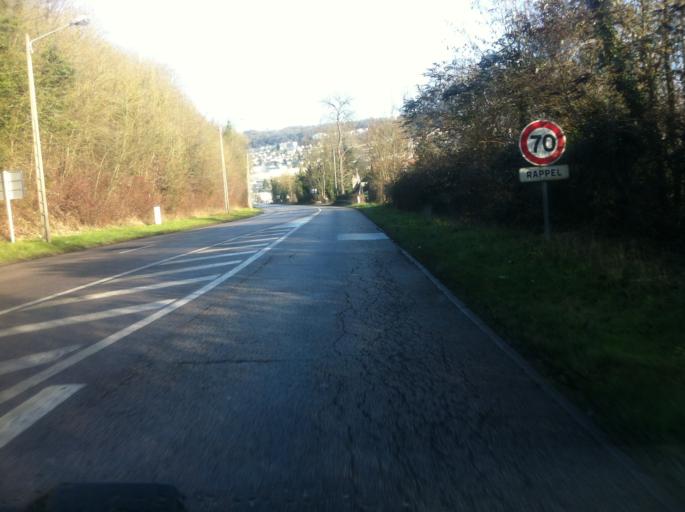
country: FR
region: Haute-Normandie
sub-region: Departement de la Seine-Maritime
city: Canteleu
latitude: 49.4459
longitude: 1.0437
